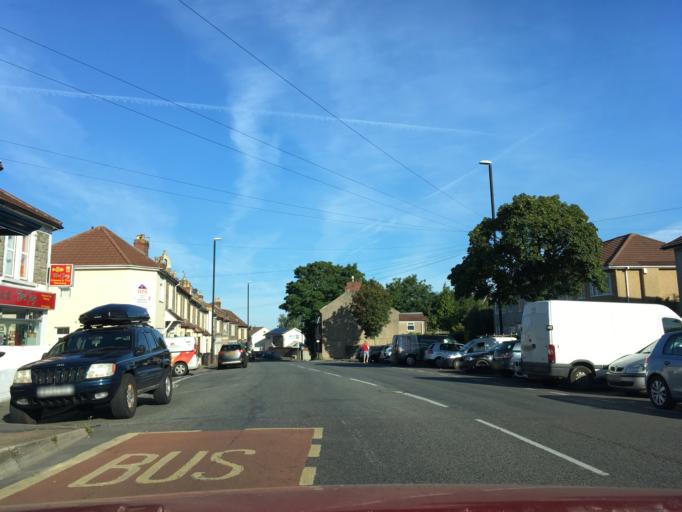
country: GB
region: England
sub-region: South Gloucestershire
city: Kingswood
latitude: 51.4546
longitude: -2.5269
